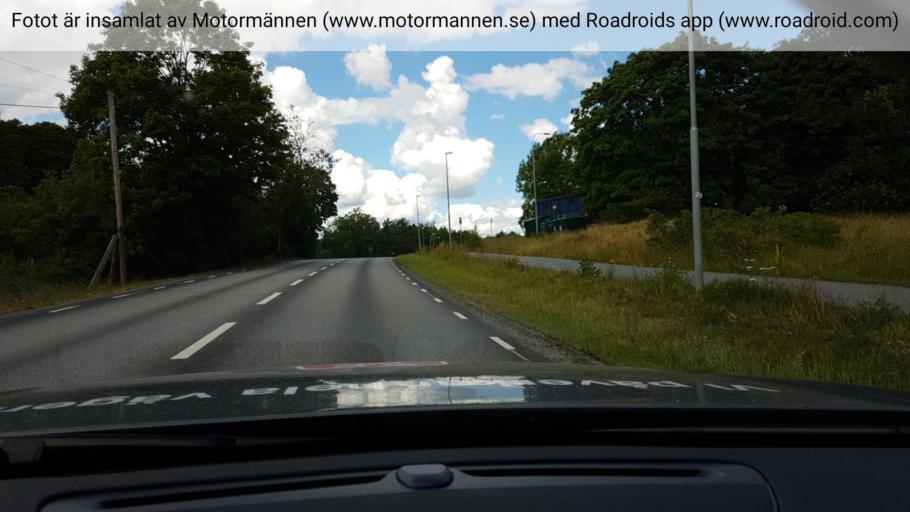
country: SE
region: Stockholm
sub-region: Varmdo Kommun
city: Hemmesta
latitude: 59.3285
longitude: 18.5018
